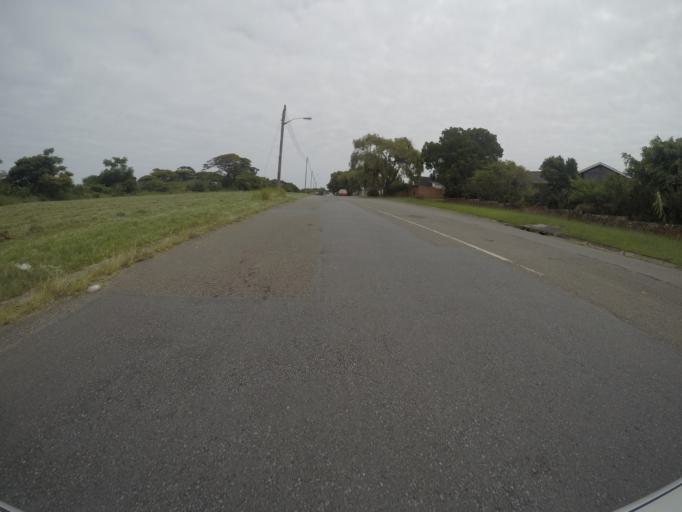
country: ZA
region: Eastern Cape
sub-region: Buffalo City Metropolitan Municipality
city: East London
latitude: -32.9748
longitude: 27.9446
